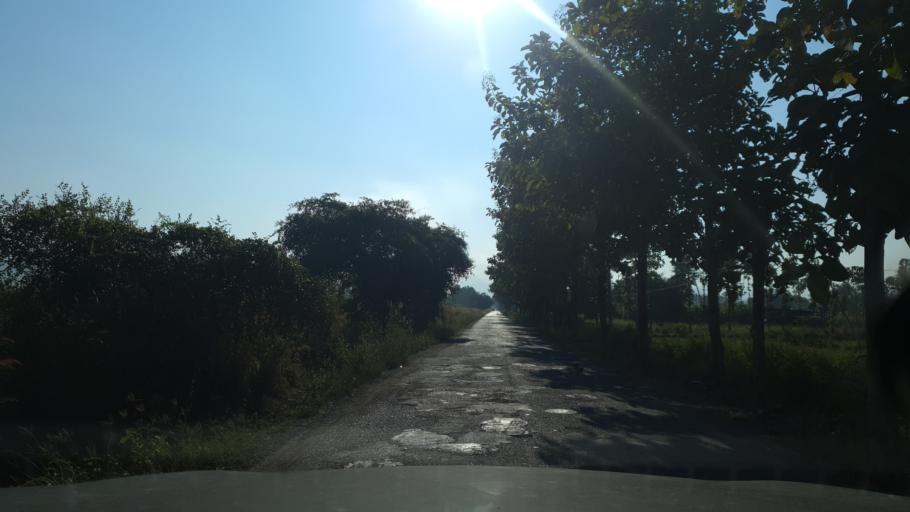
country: TH
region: Chiang Mai
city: San Kamphaeng
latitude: 18.6971
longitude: 99.1486
